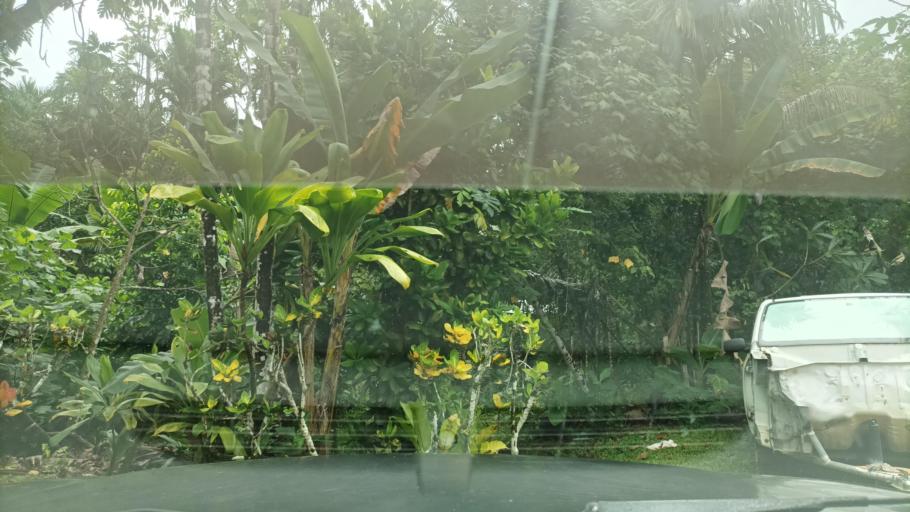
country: FM
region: Yap
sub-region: Rumung Municipality
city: Rumung
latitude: 9.5594
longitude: 138.1961
